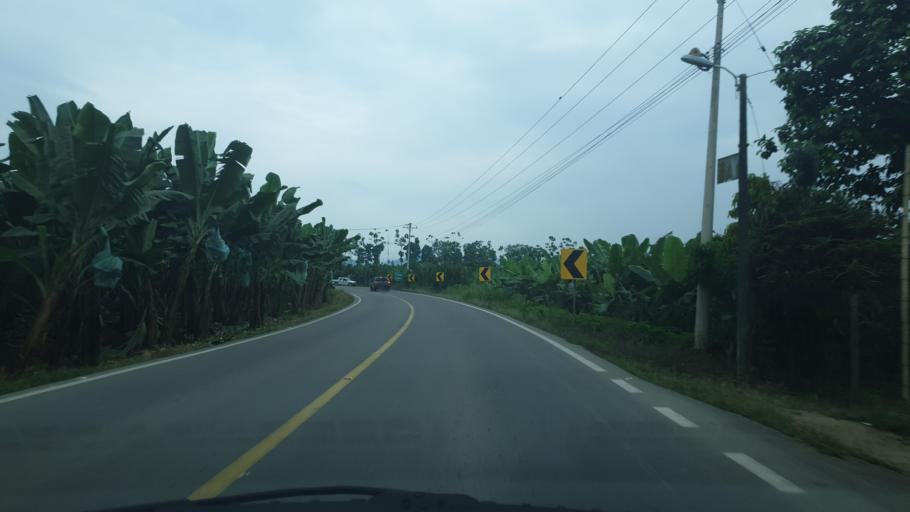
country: EC
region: El Oro
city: Pasaje
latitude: -3.3540
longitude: -79.8185
